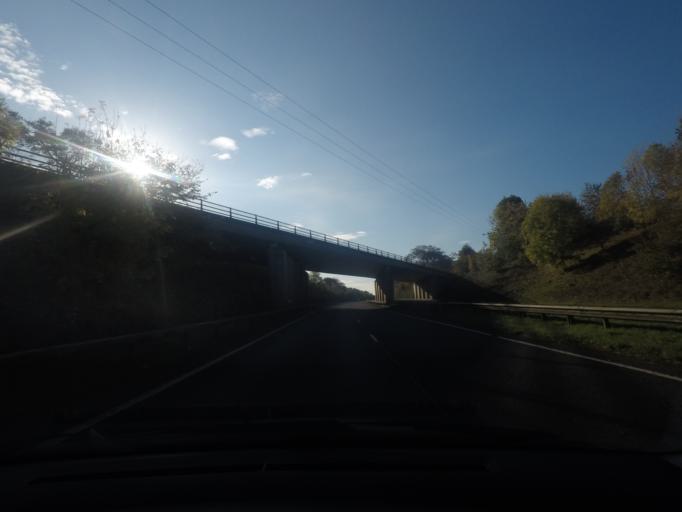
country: GB
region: England
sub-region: North Lincolnshire
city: Barton upon Humber
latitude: 53.6637
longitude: -0.4486
